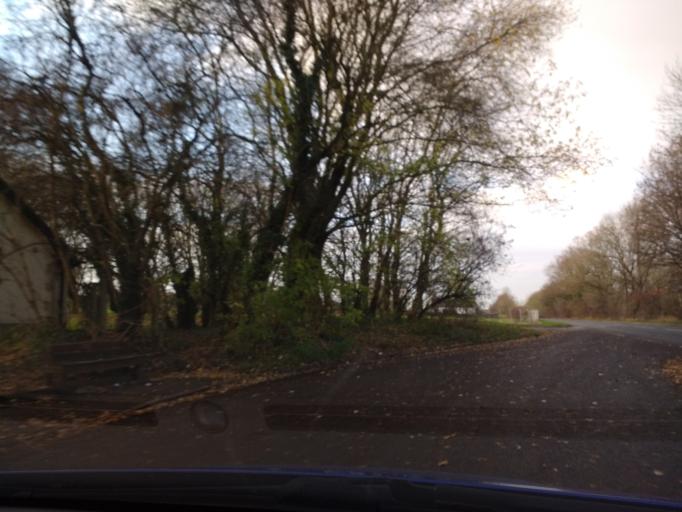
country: GB
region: England
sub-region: Lancashire
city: Caton
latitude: 54.0789
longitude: -2.7016
